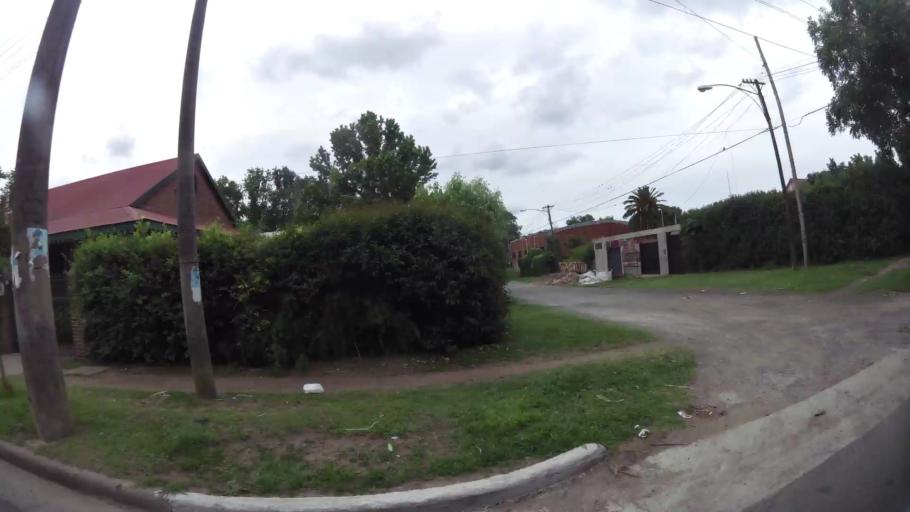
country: AR
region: Buenos Aires
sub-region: Partido de Campana
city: Campana
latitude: -34.1581
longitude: -58.9655
